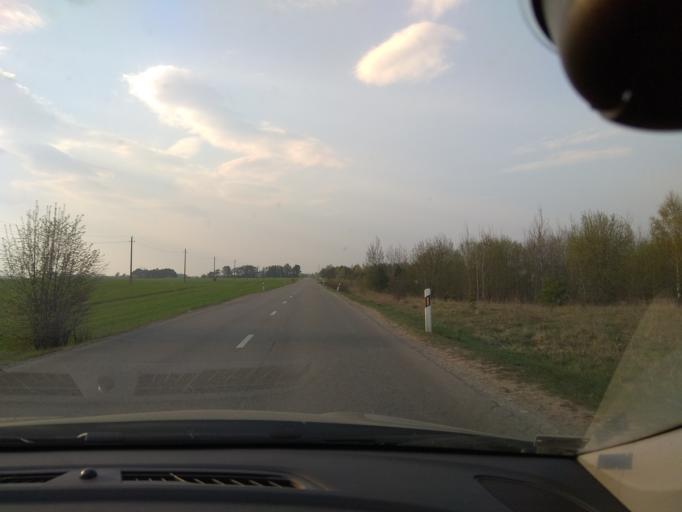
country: LT
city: Grigiskes
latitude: 54.6150
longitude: 25.1185
